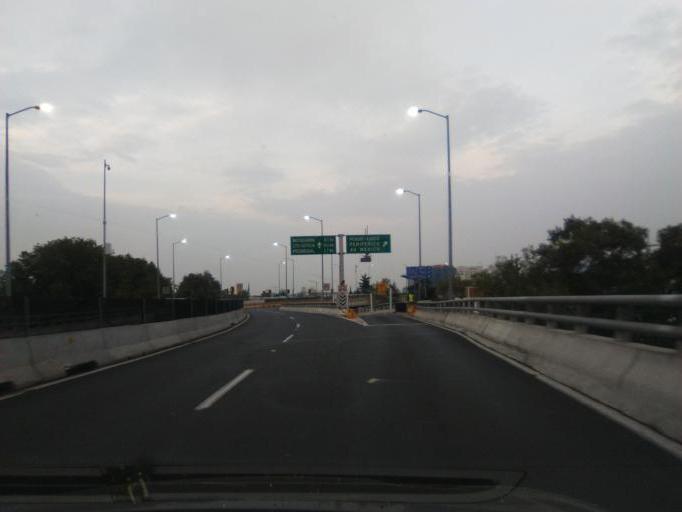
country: MX
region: Mexico City
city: Magdalena Contreras
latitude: 19.3225
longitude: -99.2248
